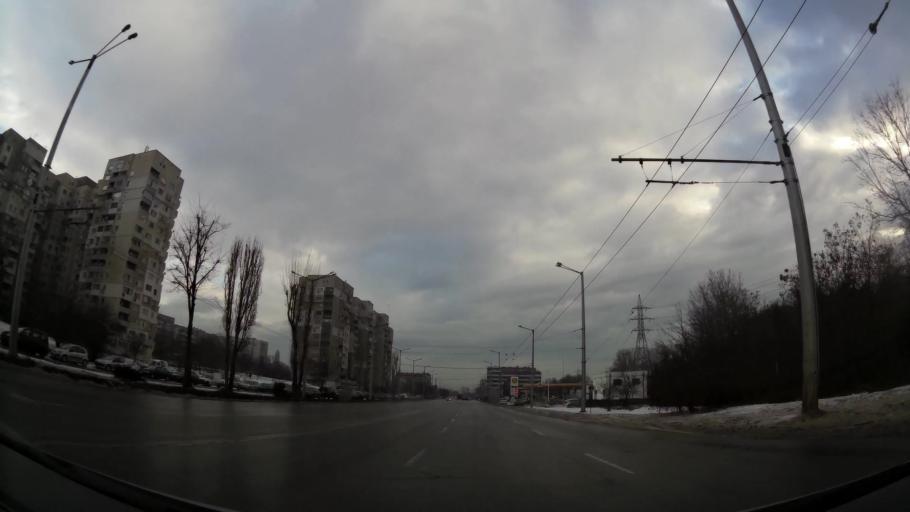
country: BG
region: Sofia-Capital
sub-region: Stolichna Obshtina
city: Sofia
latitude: 42.7134
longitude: 23.2752
